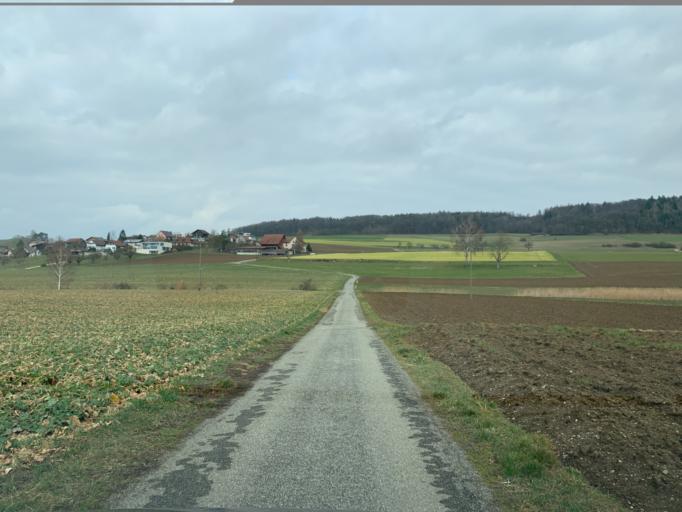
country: CH
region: Thurgau
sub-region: Frauenfeld District
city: Diessenhofen
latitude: 47.6990
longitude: 8.7273
